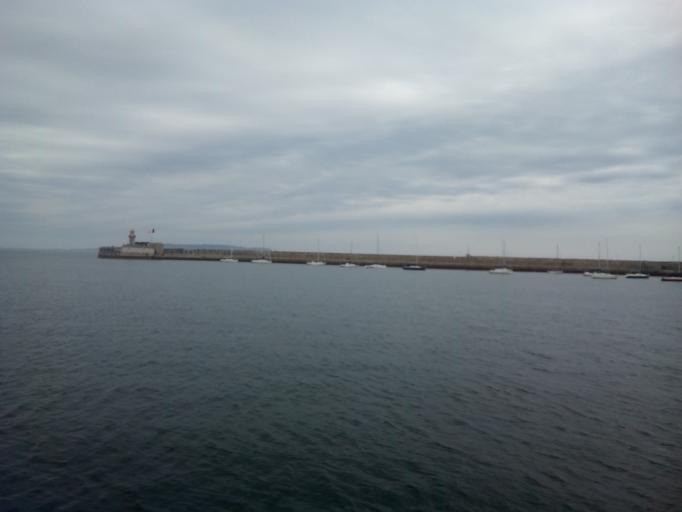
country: IE
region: Leinster
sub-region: Dun Laoghaire-Rathdown
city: Dun Laoghaire
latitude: 53.2990
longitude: -6.1290
